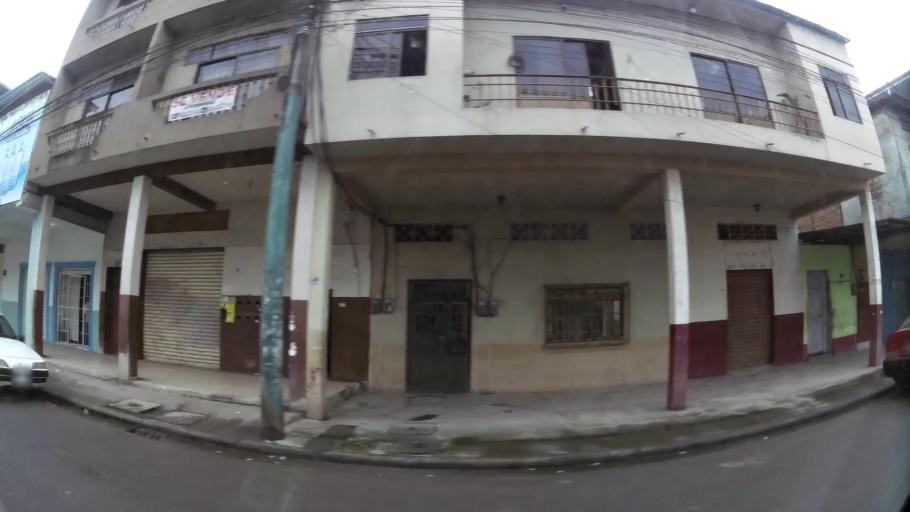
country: EC
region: El Oro
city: Pasaje
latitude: -3.3278
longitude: -79.8049
